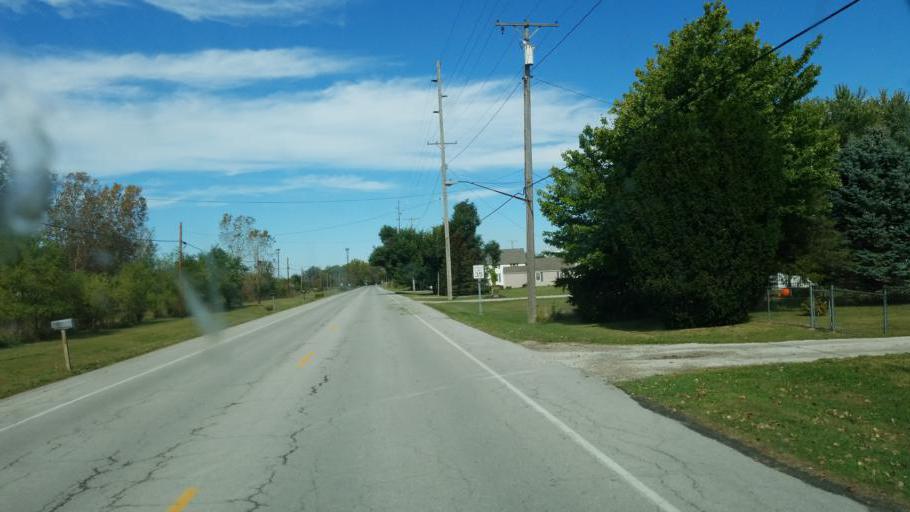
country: US
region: Ohio
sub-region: Erie County
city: Huron
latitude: 41.3800
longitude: -82.5478
